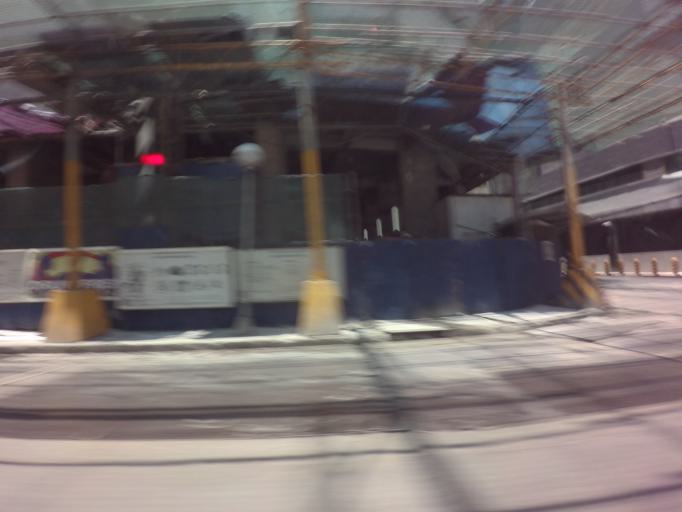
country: PH
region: Metro Manila
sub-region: Makati City
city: Makati City
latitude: 14.5613
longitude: 121.0224
